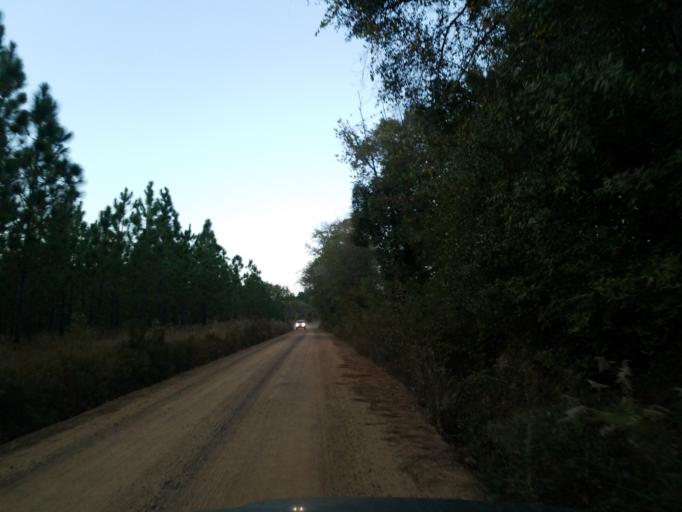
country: US
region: Georgia
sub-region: Turner County
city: Ashburn
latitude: 31.7324
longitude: -83.4839
